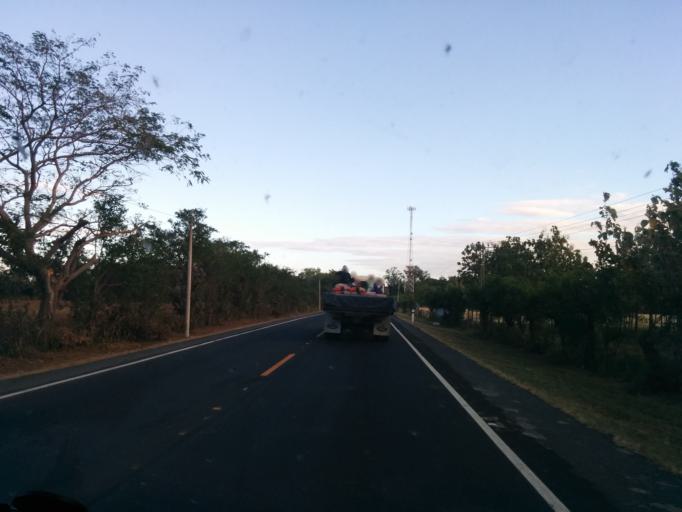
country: NI
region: Leon
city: Leon
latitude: 12.3394
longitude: -86.8153
